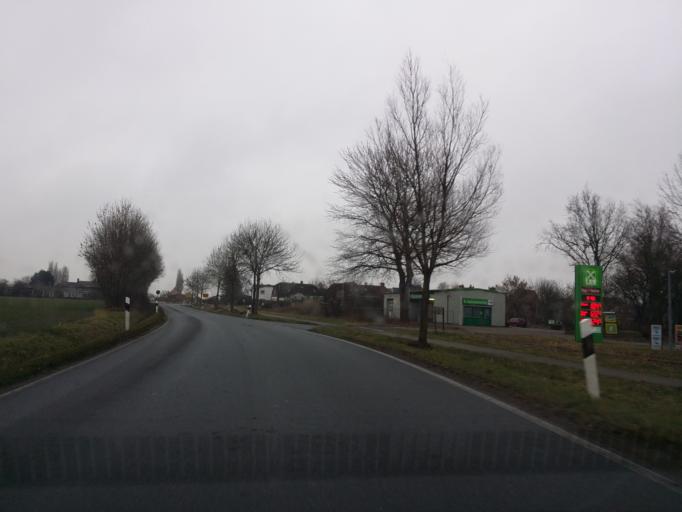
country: DE
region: Schleswig-Holstein
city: Fehmarn
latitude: 54.4540
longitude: 11.1436
